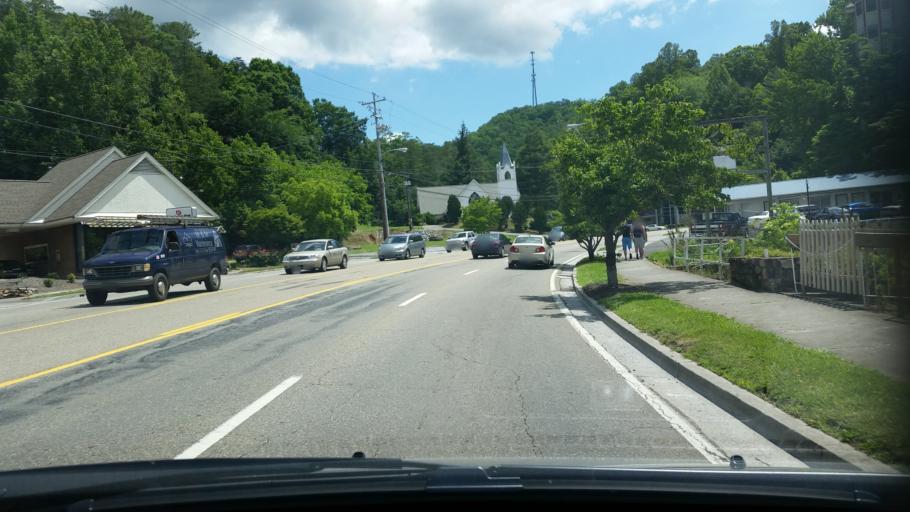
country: US
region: Tennessee
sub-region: Sevier County
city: Gatlinburg
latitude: 35.7170
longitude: -83.5018
